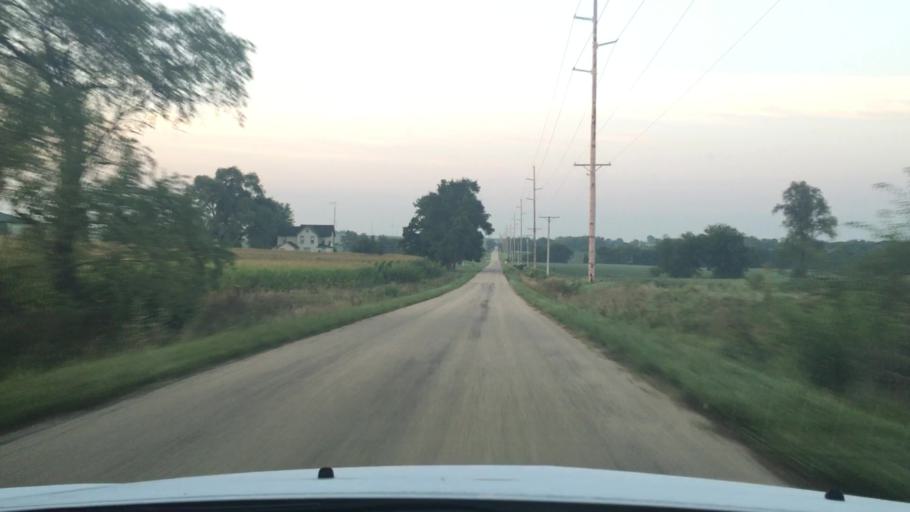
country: US
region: Illinois
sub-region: Ogle County
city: Rochelle
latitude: 41.8529
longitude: -89.0005
